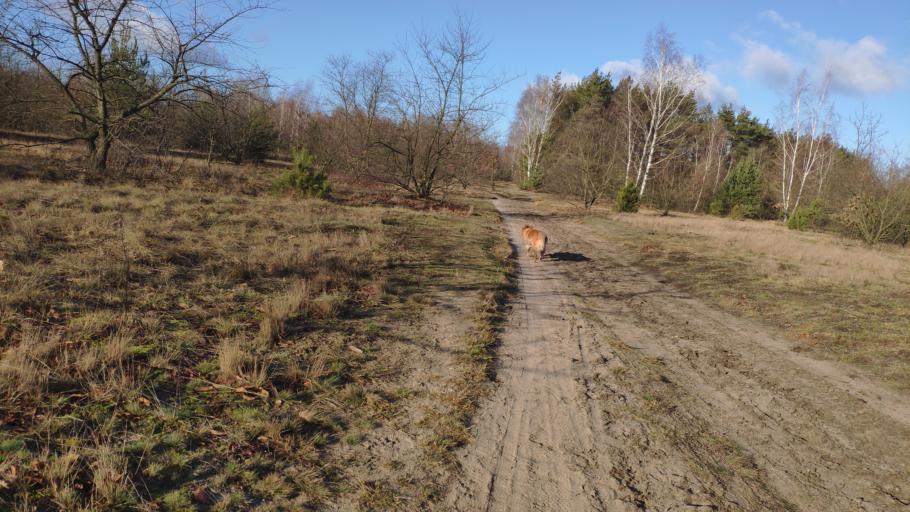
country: PL
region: Lodz Voivodeship
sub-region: Powiat pabianicki
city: Ksawerow
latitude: 51.7277
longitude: 19.4120
